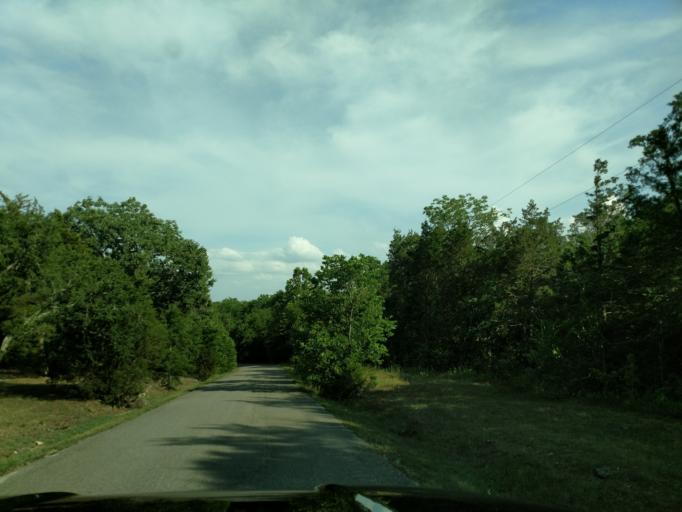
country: US
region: Missouri
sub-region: Barry County
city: Shell Knob
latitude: 36.5961
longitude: -93.5526
